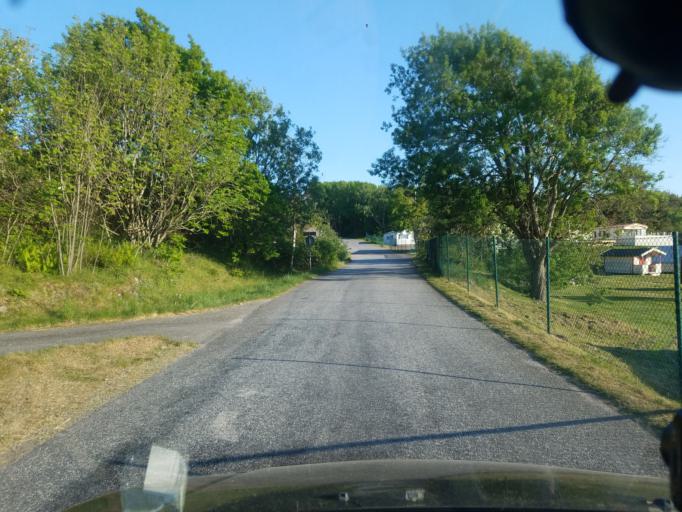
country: SE
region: Vaestra Goetaland
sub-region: Lysekils Kommun
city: Lysekil
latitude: 58.2971
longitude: 11.4487
